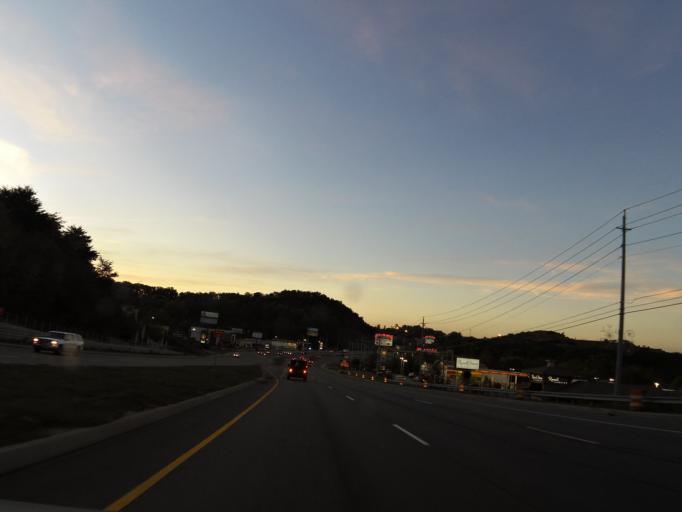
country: US
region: Tennessee
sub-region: Sevier County
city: Sevierville
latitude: 35.9749
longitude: -83.6044
